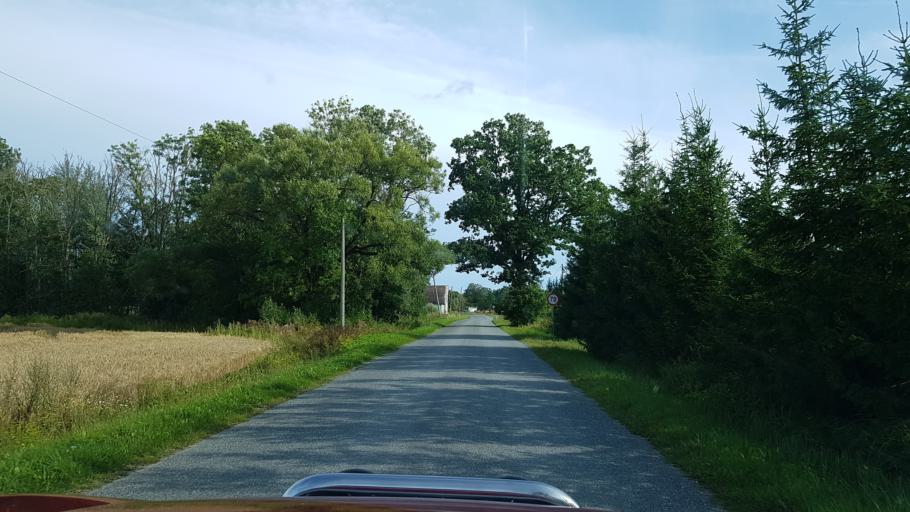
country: EE
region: Laeaene
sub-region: Lihula vald
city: Lihula
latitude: 58.4506
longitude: 23.9966
